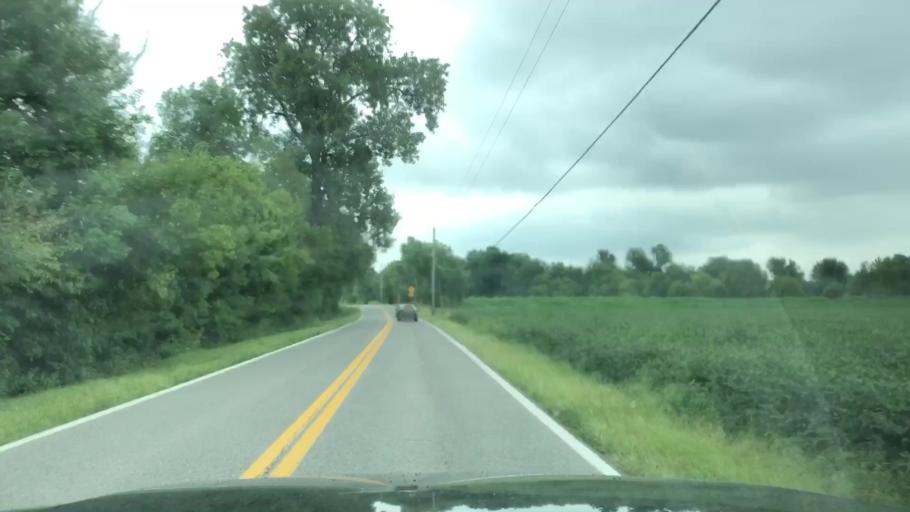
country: US
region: Missouri
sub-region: Saint Louis County
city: Bridgeton
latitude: 38.7971
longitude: -90.4223
